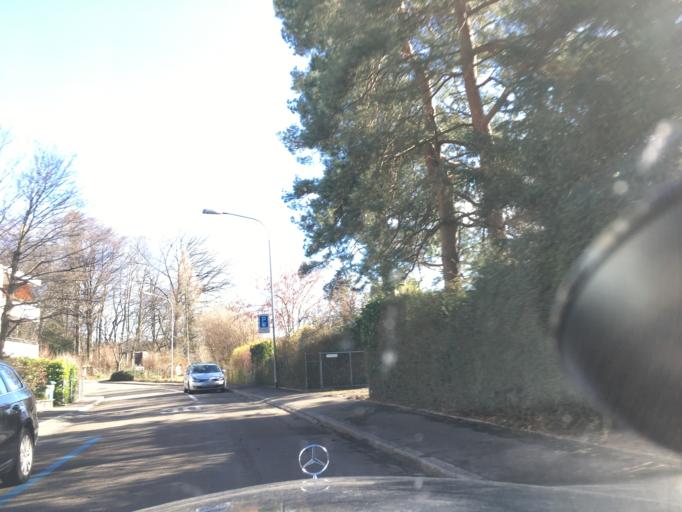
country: CH
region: Zurich
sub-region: Bezirk Zuerich
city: Zuerich (Kreis 8) / Weinegg
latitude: 47.3556
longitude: 8.5800
